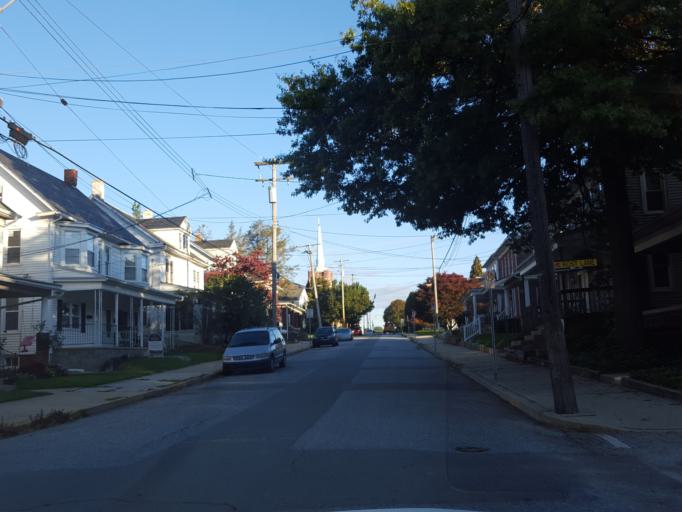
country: US
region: Pennsylvania
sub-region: York County
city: Red Lion
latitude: 39.9009
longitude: -76.6101
